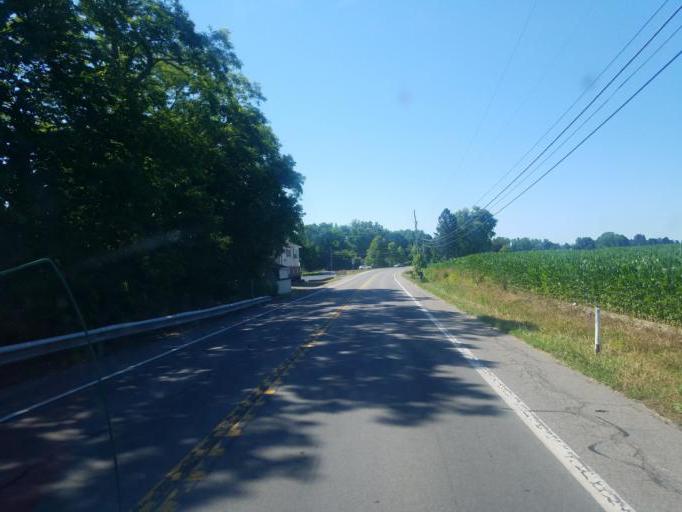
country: US
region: New York
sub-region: Ontario County
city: Phelps
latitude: 42.9871
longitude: -77.0874
